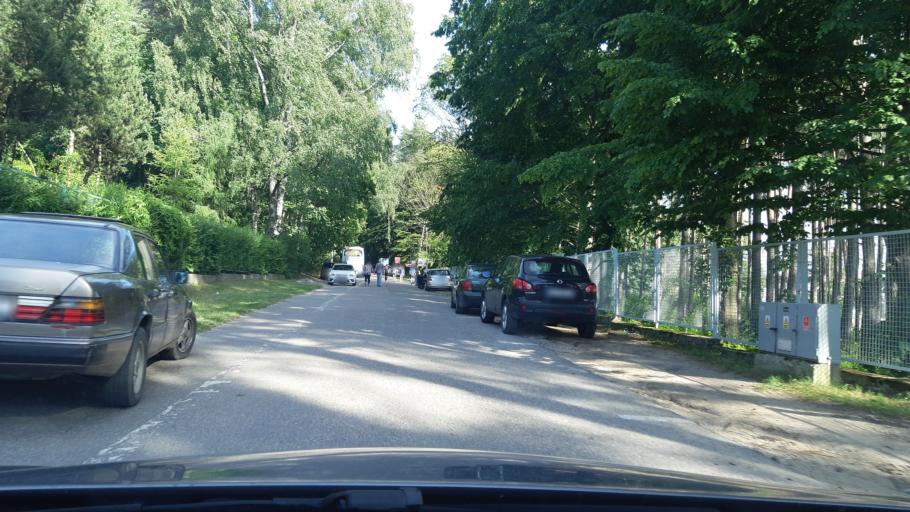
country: PL
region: Warmian-Masurian Voivodeship
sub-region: Powiat mragowski
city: Mragowo
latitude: 53.8737
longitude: 21.3212
